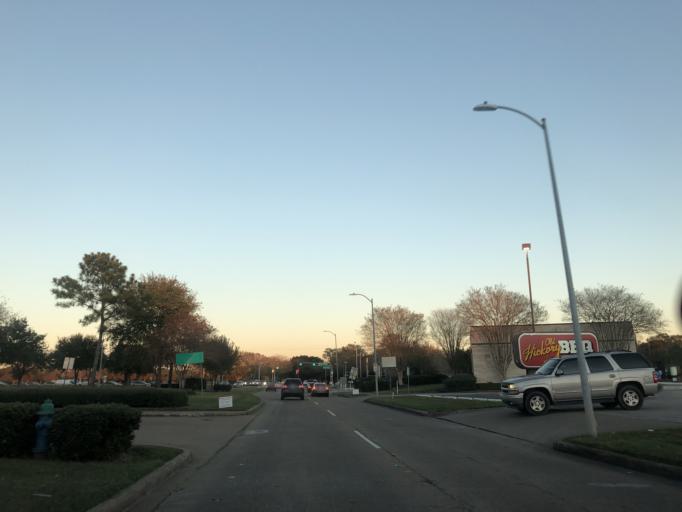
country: US
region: Texas
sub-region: Harris County
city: Bellaire
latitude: 29.6764
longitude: -95.4782
